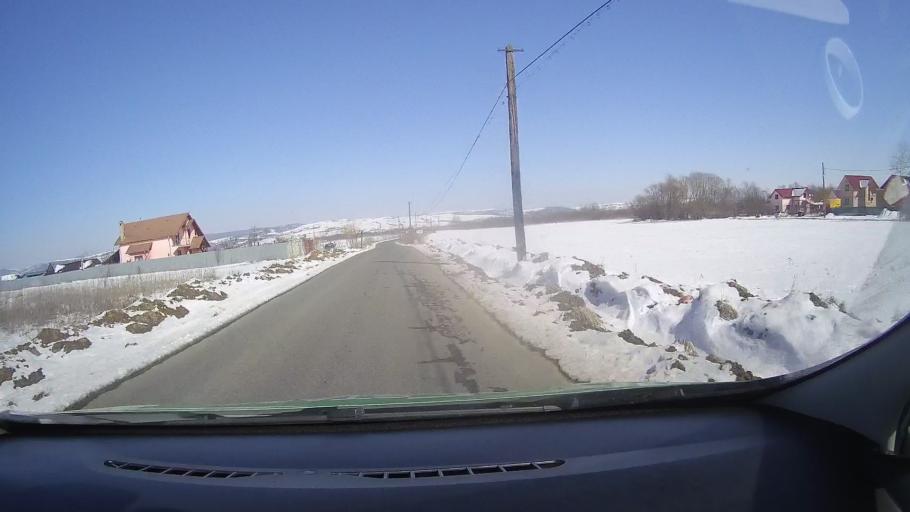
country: RO
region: Brasov
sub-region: Comuna Mandra
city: Mandra
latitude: 45.8271
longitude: 25.0106
